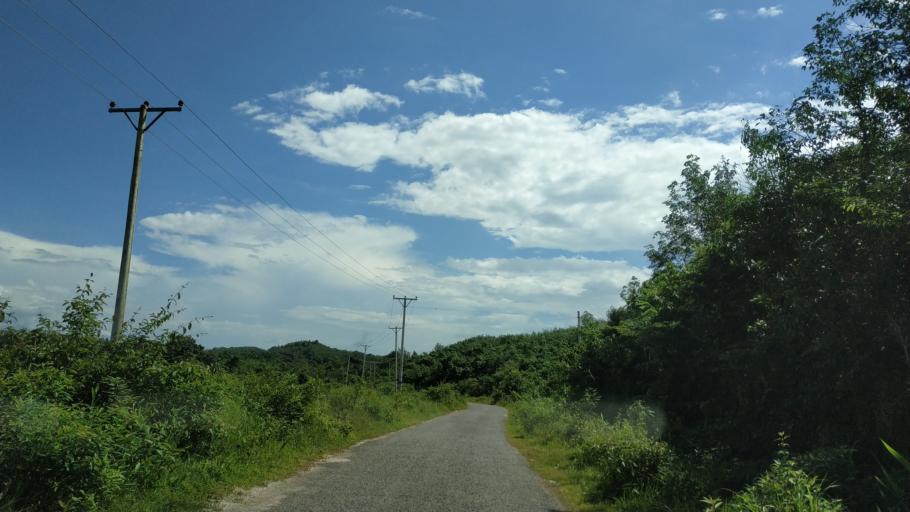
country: MM
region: Tanintharyi
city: Dawei
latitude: 14.2083
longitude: 98.1851
